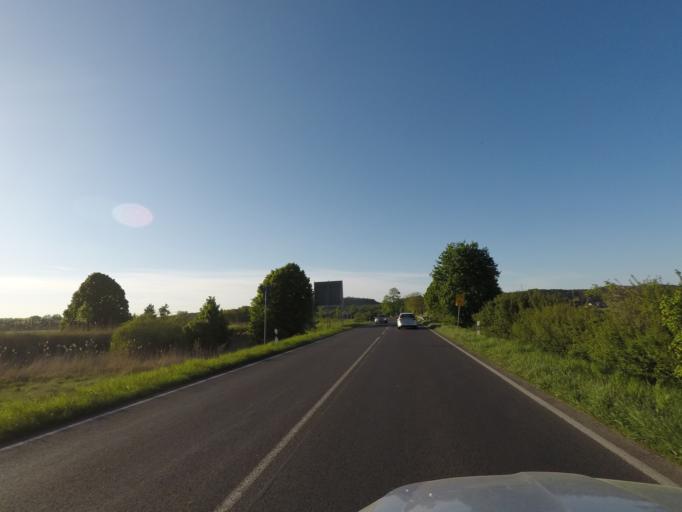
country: DE
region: Brandenburg
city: Bad Freienwalde
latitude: 52.7985
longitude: 14.0463
